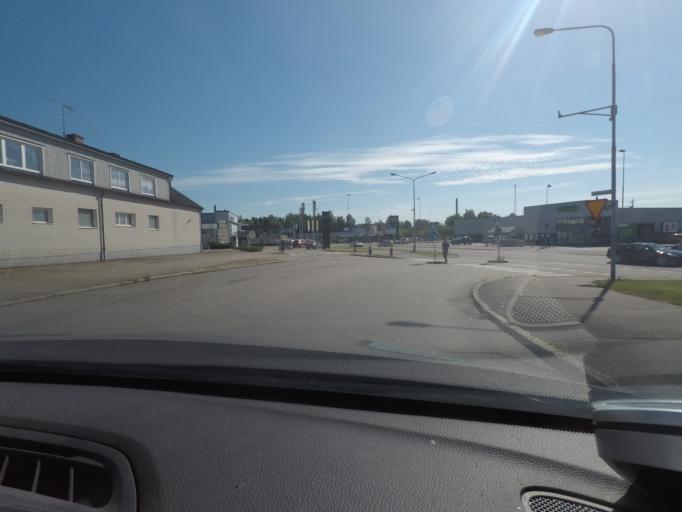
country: SE
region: Kronoberg
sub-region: Markaryds Kommun
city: Markaryd
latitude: 56.4576
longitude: 13.5945
